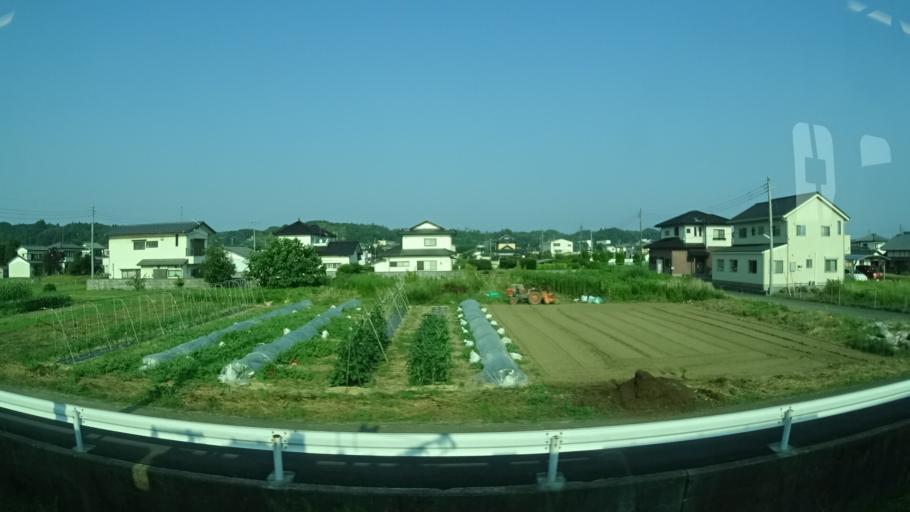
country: JP
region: Ibaraki
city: Kitaibaraki
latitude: 36.8410
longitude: 140.7775
